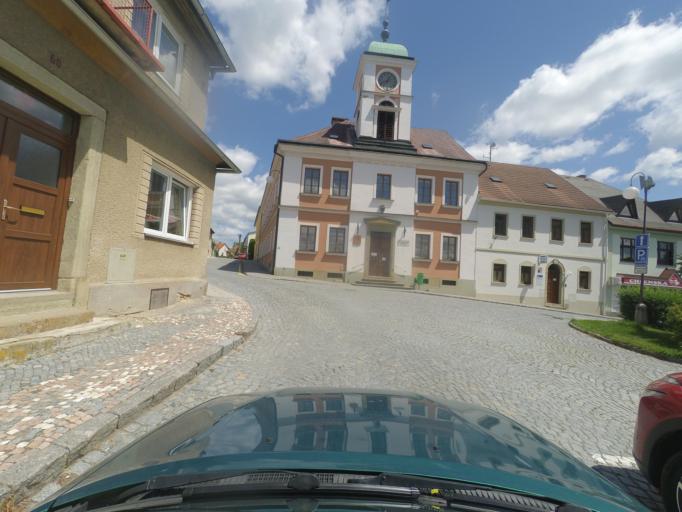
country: CZ
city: Solnice
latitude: 50.2044
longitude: 16.2377
